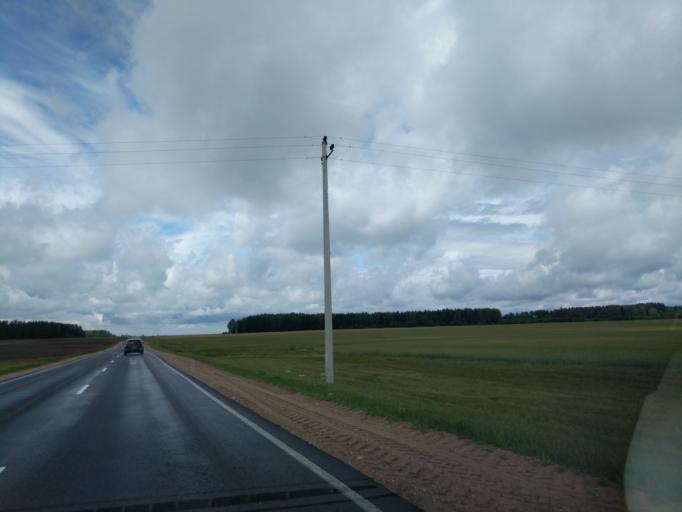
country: BY
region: Minsk
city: Il'ya
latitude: 54.3774
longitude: 27.3796
